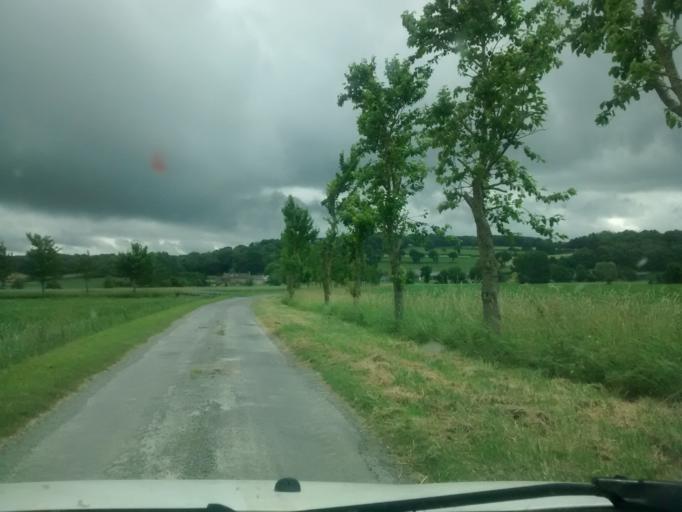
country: FR
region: Brittany
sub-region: Departement d'Ille-et-Vilaine
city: Saint-Broladre
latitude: 48.5847
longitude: -1.6841
